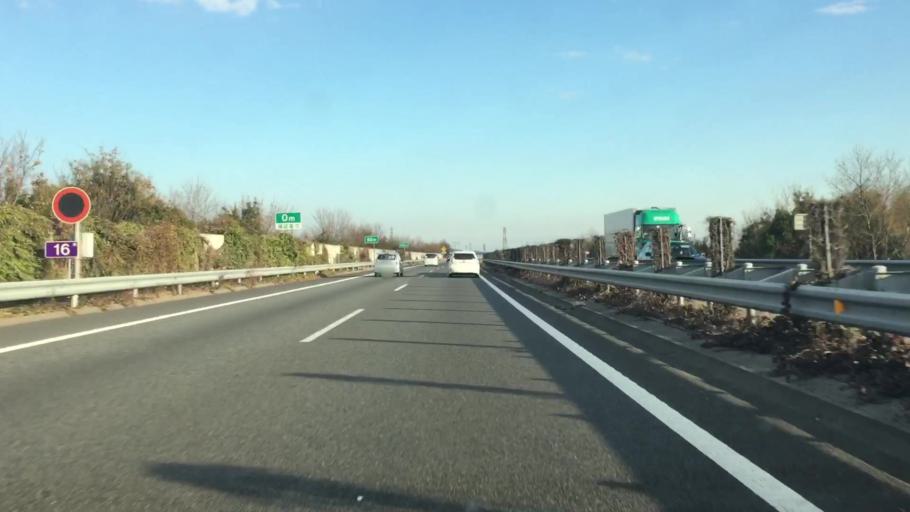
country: JP
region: Gunma
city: Isesaki
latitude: 36.3506
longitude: 139.2365
